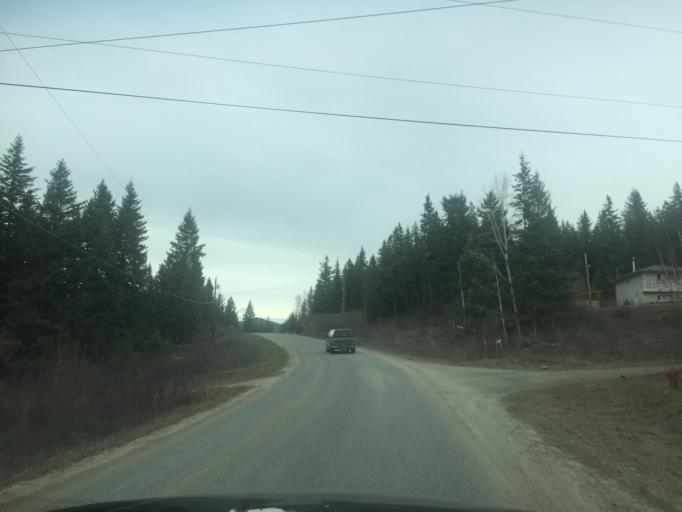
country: CA
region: British Columbia
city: Kamloops
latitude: 51.3194
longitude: -120.1476
